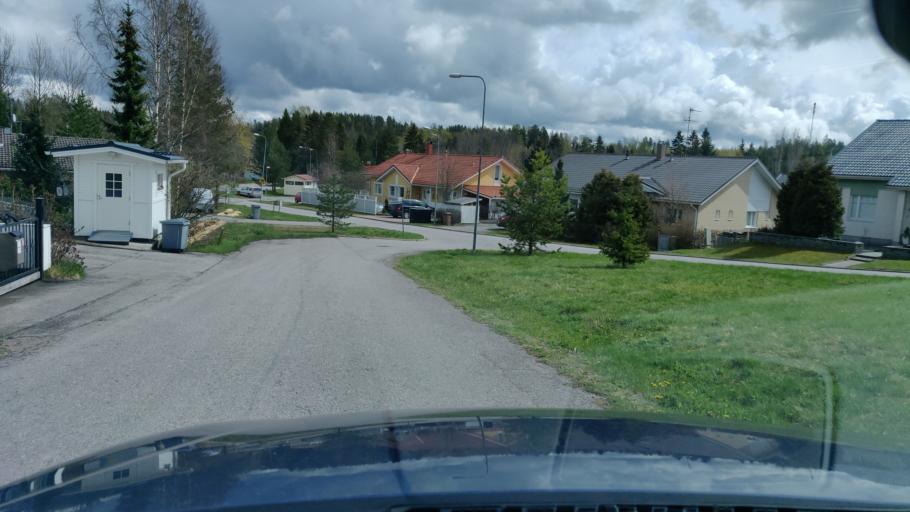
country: FI
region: Uusimaa
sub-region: Helsinki
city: Nurmijaervi
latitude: 60.3632
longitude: 24.7366
